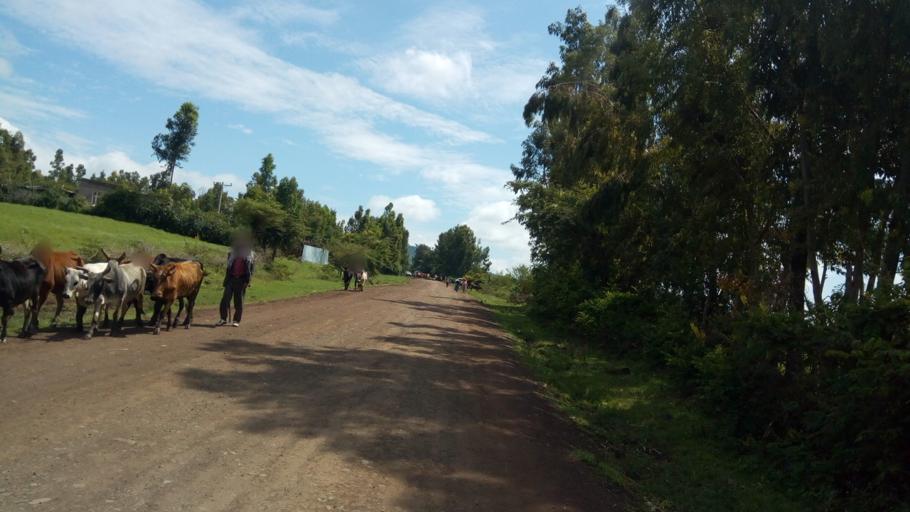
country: ET
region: Oromiya
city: Bishoftu
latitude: 8.8444
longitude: 39.0162
